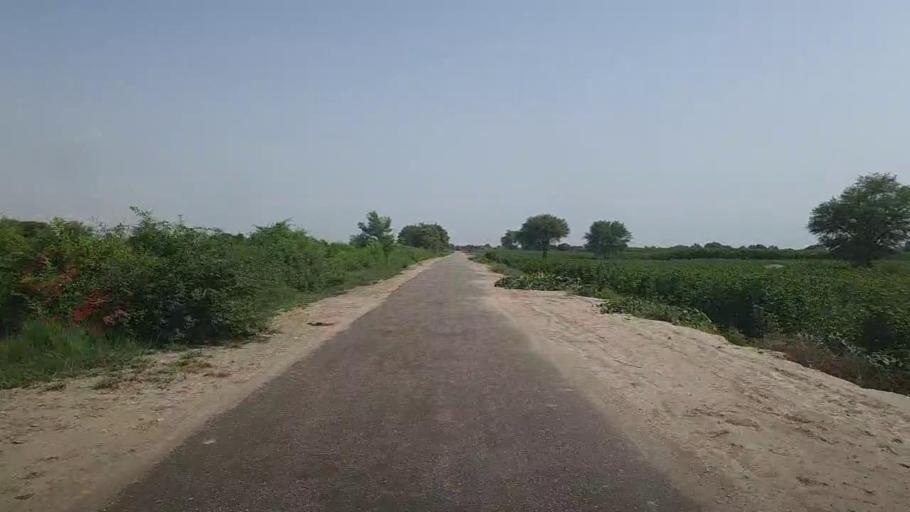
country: PK
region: Sindh
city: Pad Idan
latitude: 26.8371
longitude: 68.3307
